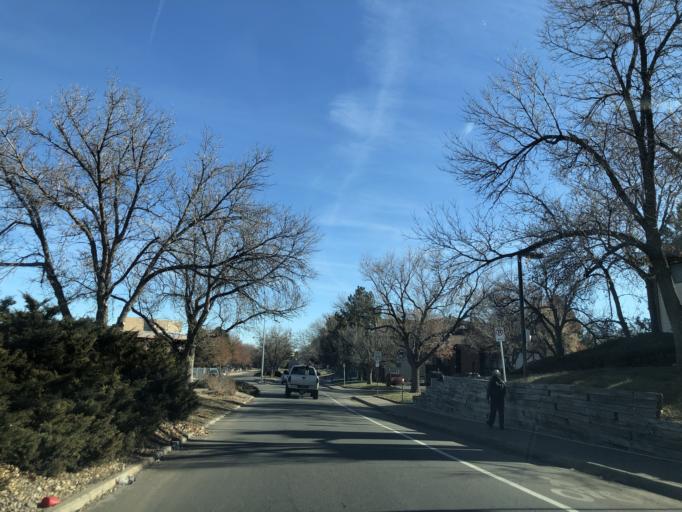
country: US
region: Colorado
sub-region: Adams County
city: Aurora
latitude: 39.7197
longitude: -104.8193
